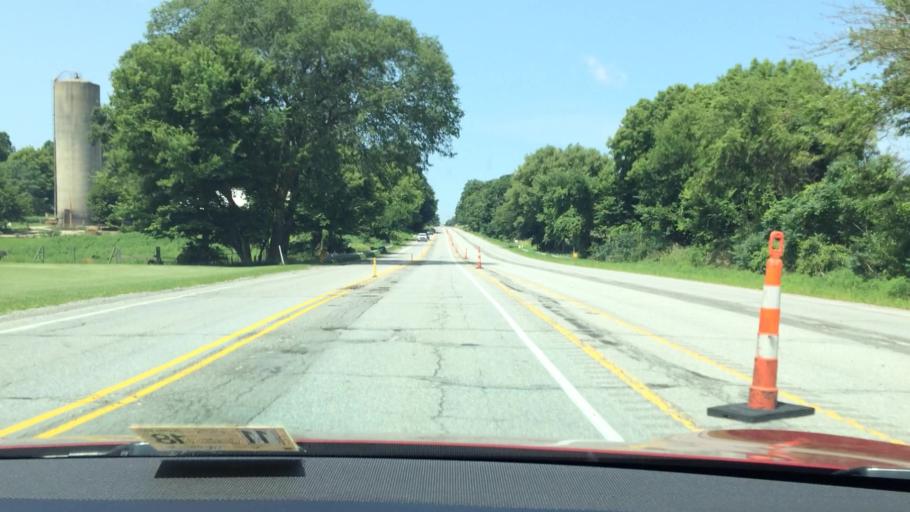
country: US
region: Indiana
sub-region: LaPorte County
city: LaPorte
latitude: 41.6736
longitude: -86.6480
